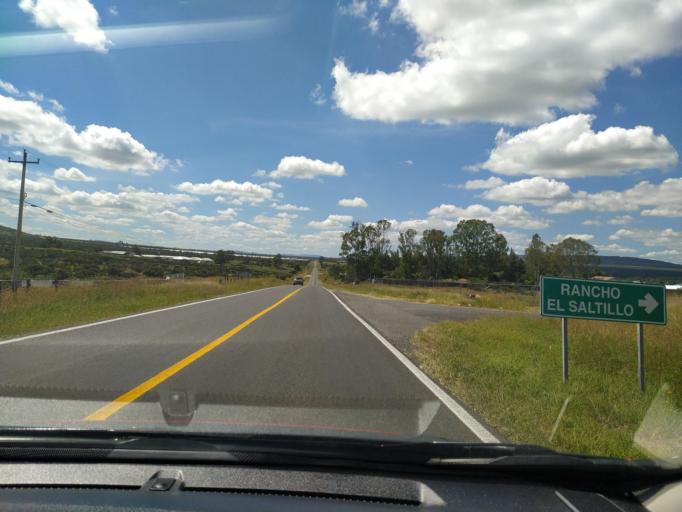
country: MX
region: Jalisco
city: San Miguel el Alto
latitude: 21.0226
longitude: -102.4418
